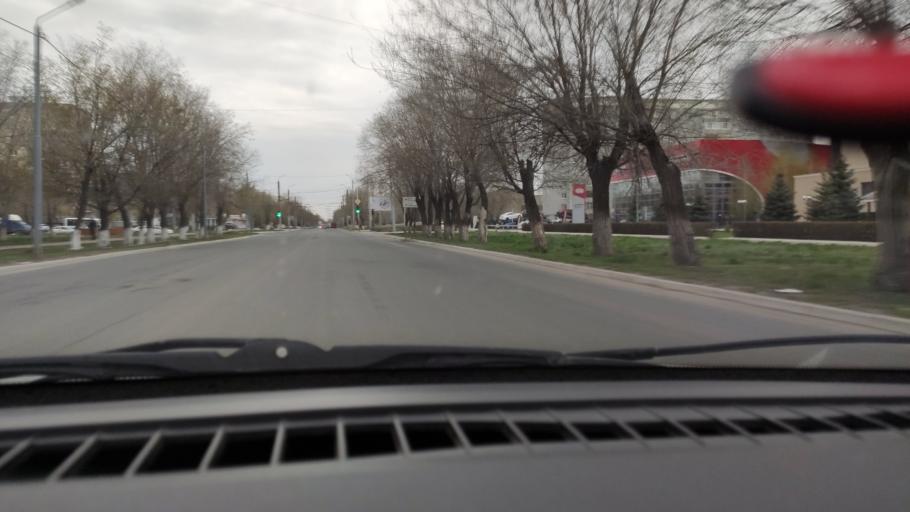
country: RU
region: Orenburg
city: Orenburg
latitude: 51.8453
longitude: 55.1332
